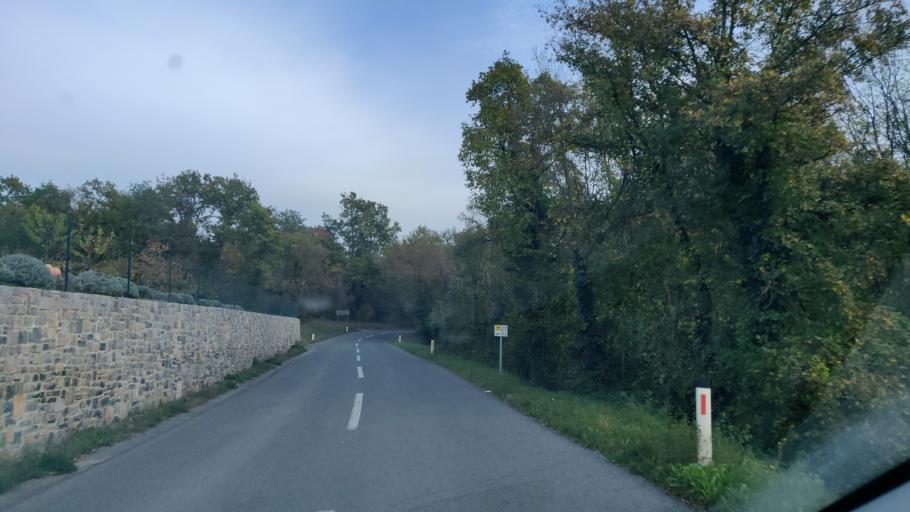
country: SI
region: Komen
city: Komen
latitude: 45.8170
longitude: 13.7769
